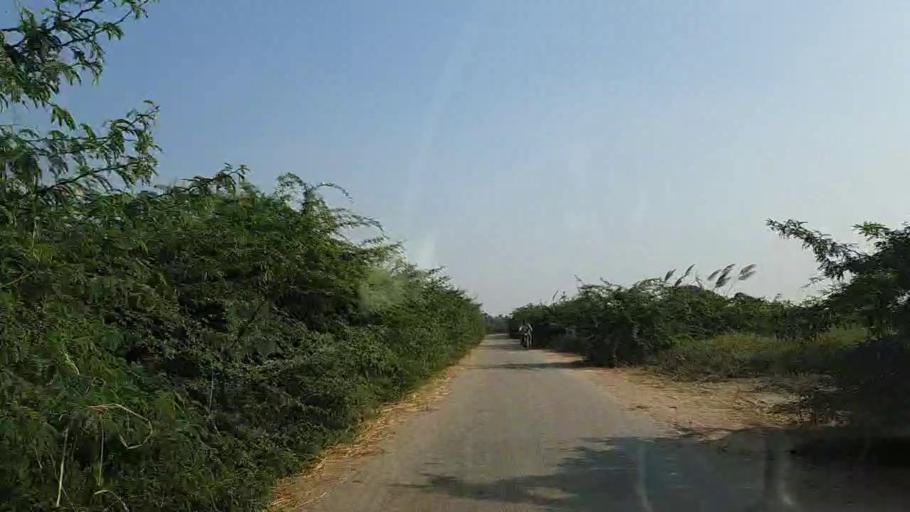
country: PK
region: Sindh
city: Mirpur Sakro
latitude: 24.6212
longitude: 67.6586
